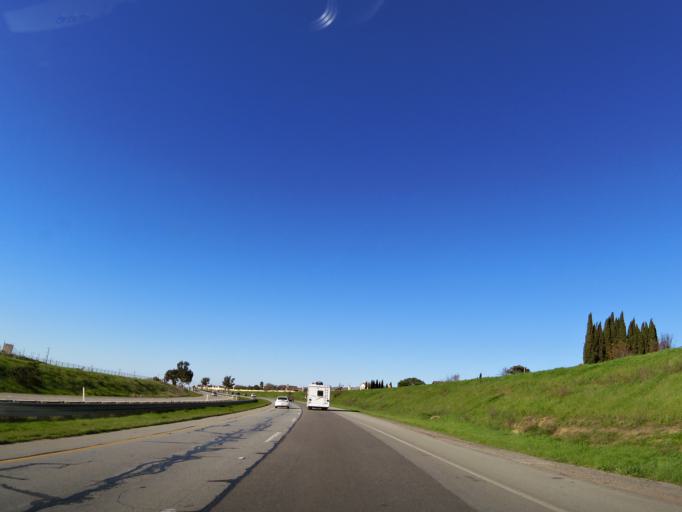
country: US
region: California
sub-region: Monterey County
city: Gonzales
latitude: 36.5164
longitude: -121.4396
